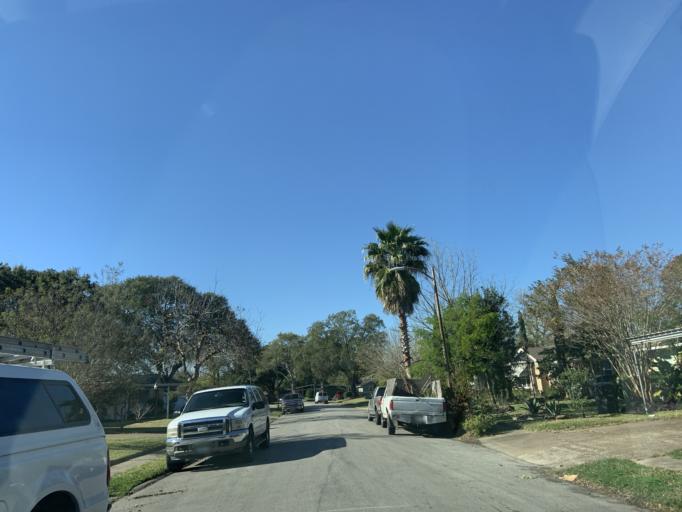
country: US
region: Texas
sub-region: Harris County
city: Bellaire
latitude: 29.6953
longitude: -95.5034
